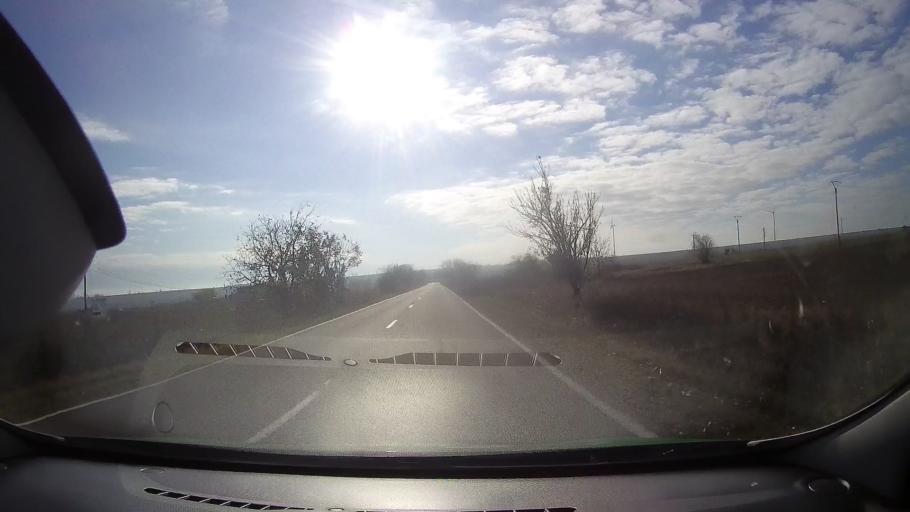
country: RO
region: Tulcea
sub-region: Comuna Mahmudia
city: Mahmudia
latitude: 45.0777
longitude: 29.0793
